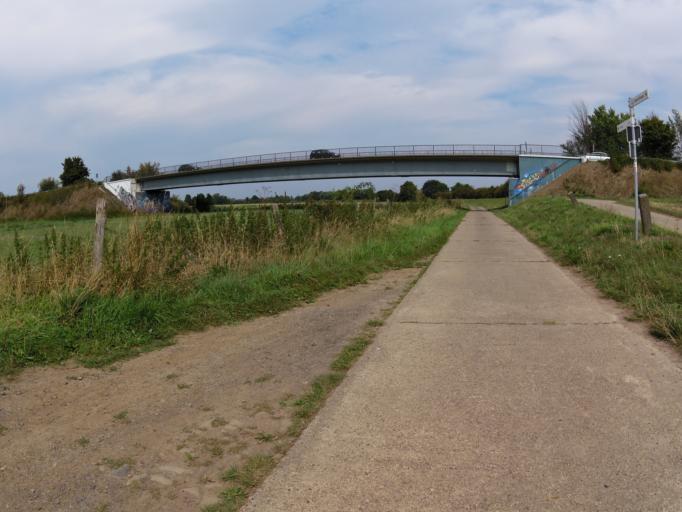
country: DE
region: Lower Saxony
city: Landesbergen
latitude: 52.5589
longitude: 9.1148
